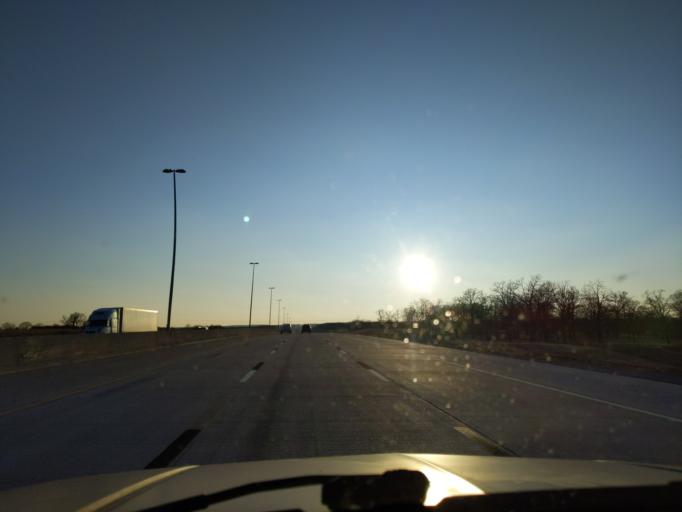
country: US
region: Oklahoma
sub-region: Creek County
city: Kellyville
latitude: 35.9408
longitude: -96.2584
